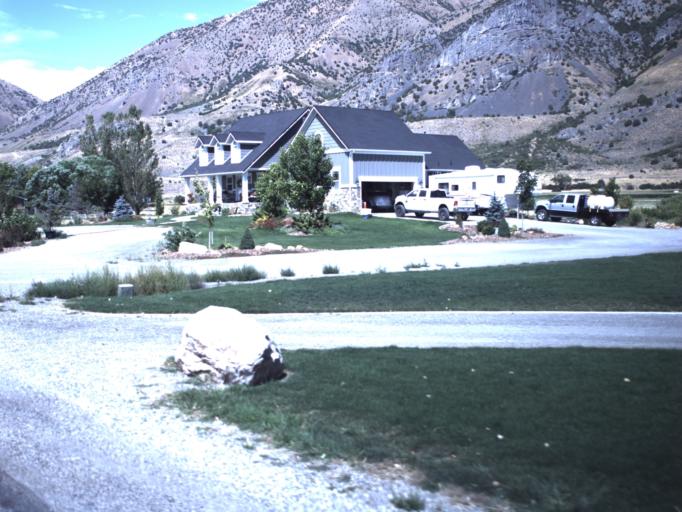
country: US
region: Utah
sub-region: Box Elder County
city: Honeyville
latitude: 41.6885
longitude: -112.0899
